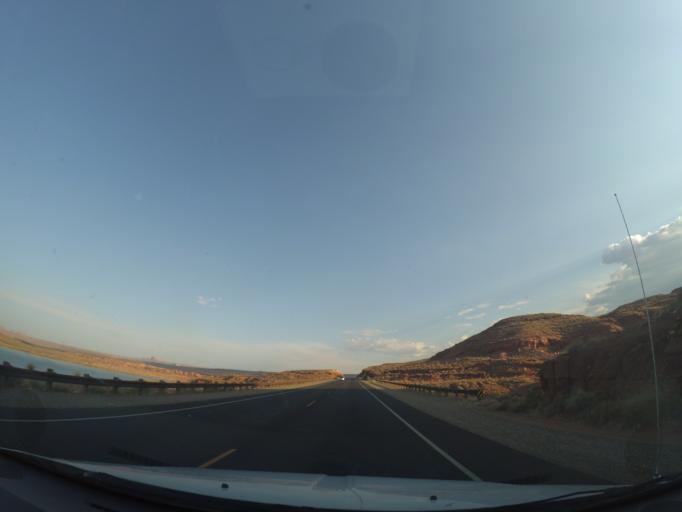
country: US
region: Arizona
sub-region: Coconino County
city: Page
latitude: 36.9756
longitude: -111.4921
